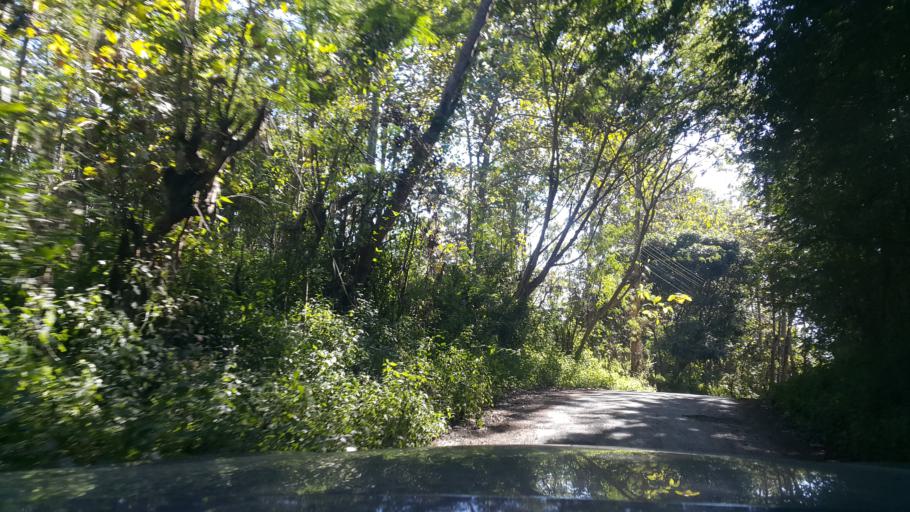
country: TH
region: Chiang Mai
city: Mae On
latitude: 18.7759
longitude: 99.2617
